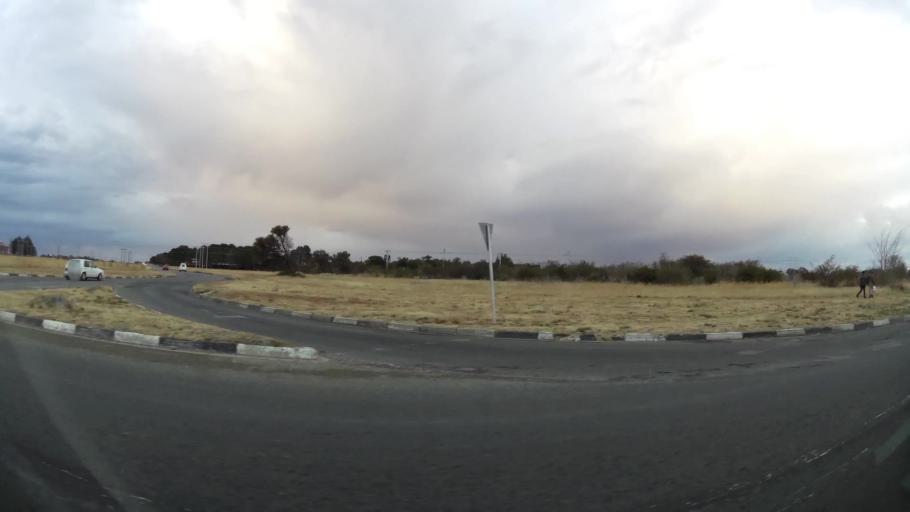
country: ZA
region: Orange Free State
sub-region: Lejweleputswa District Municipality
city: Welkom
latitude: -27.9650
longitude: 26.7607
